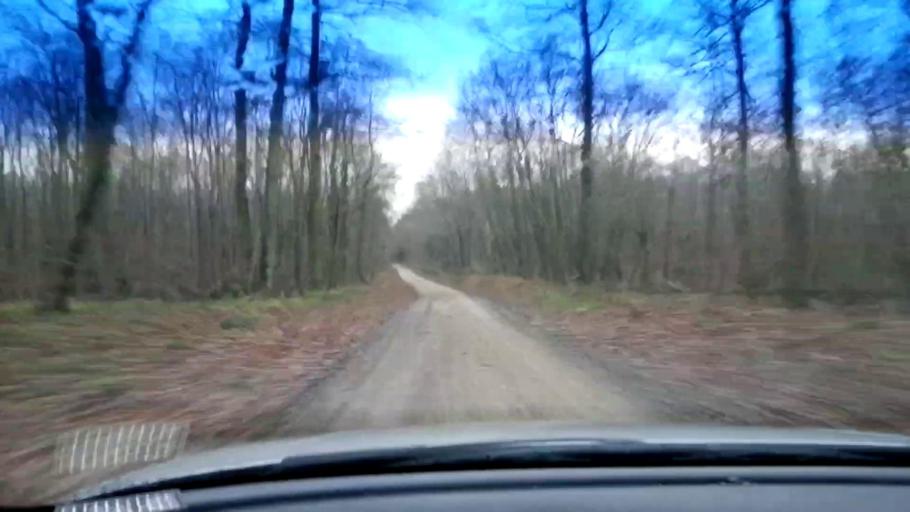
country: DE
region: Bavaria
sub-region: Upper Franconia
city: Schesslitz
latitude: 49.9441
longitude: 11.0248
